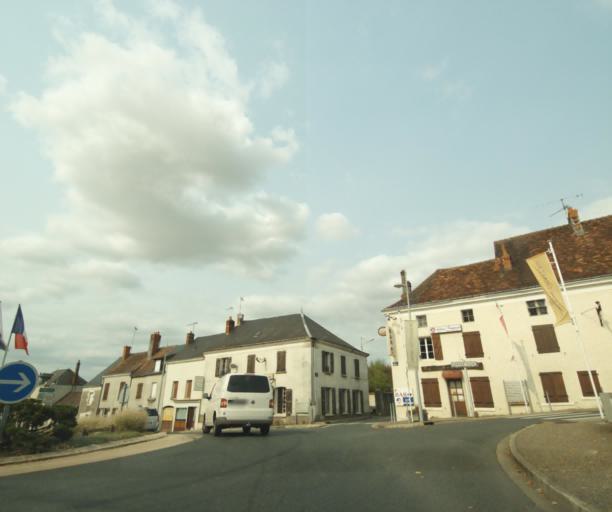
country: FR
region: Centre
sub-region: Departement de l'Indre
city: Chatillon-sur-Indre
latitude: 46.9888
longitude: 1.1717
